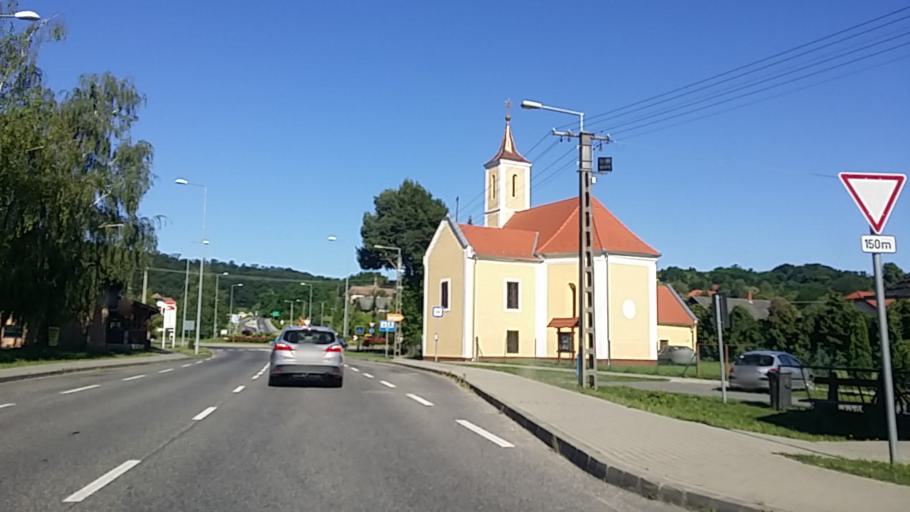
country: HU
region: Zala
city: Heviz
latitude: 46.8053
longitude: 17.0979
